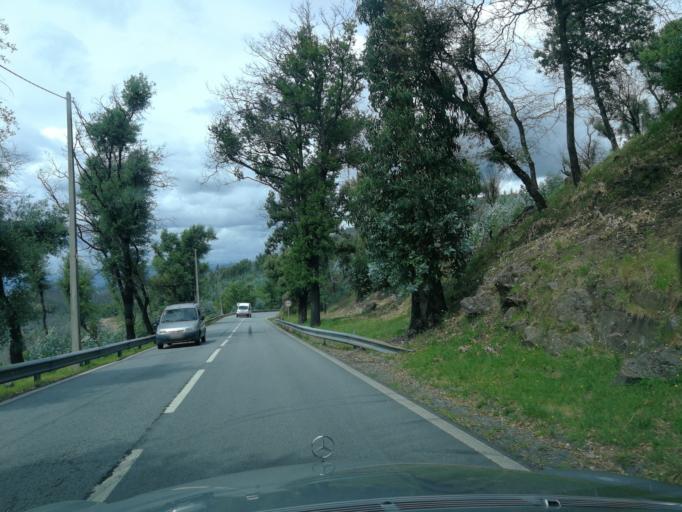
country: PT
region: Braga
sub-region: Braga
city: Braga
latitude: 41.5224
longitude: -8.3893
